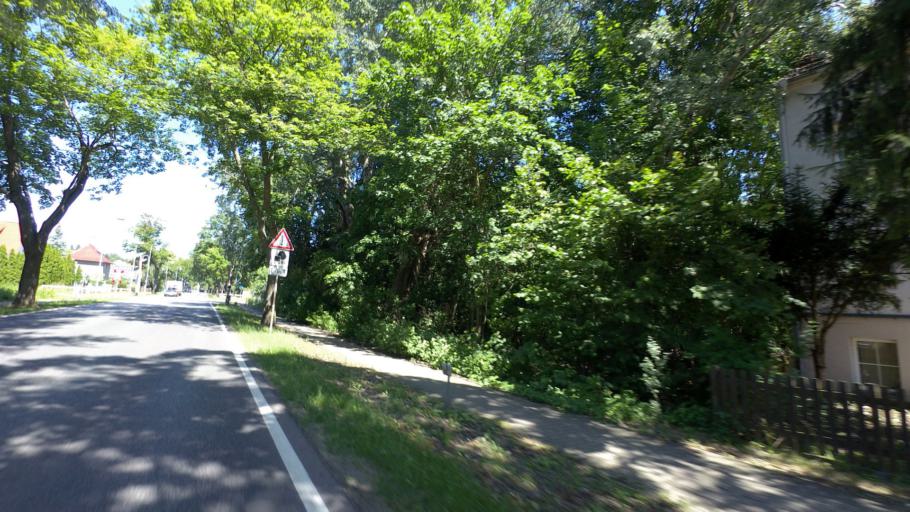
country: DE
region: Brandenburg
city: Zossen
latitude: 52.2414
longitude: 13.4494
